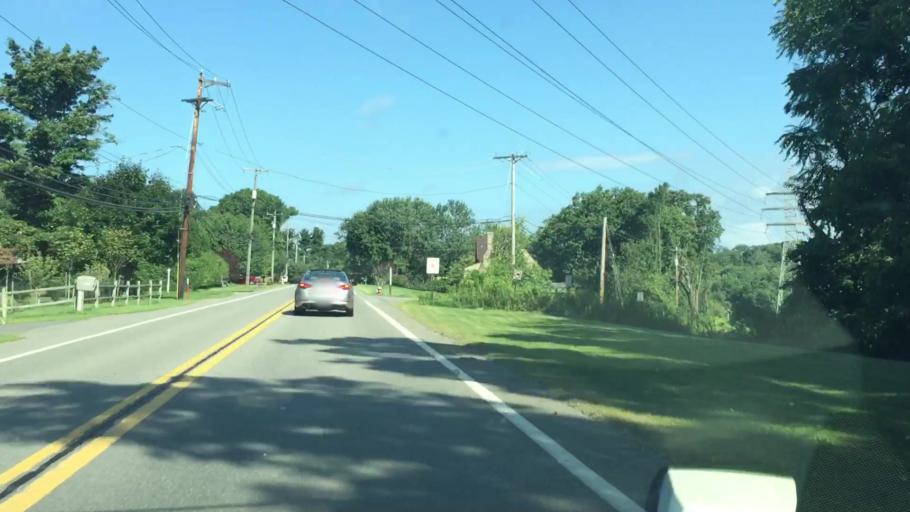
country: US
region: Pennsylvania
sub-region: Allegheny County
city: Franklin Park
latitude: 40.5691
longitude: -80.1040
